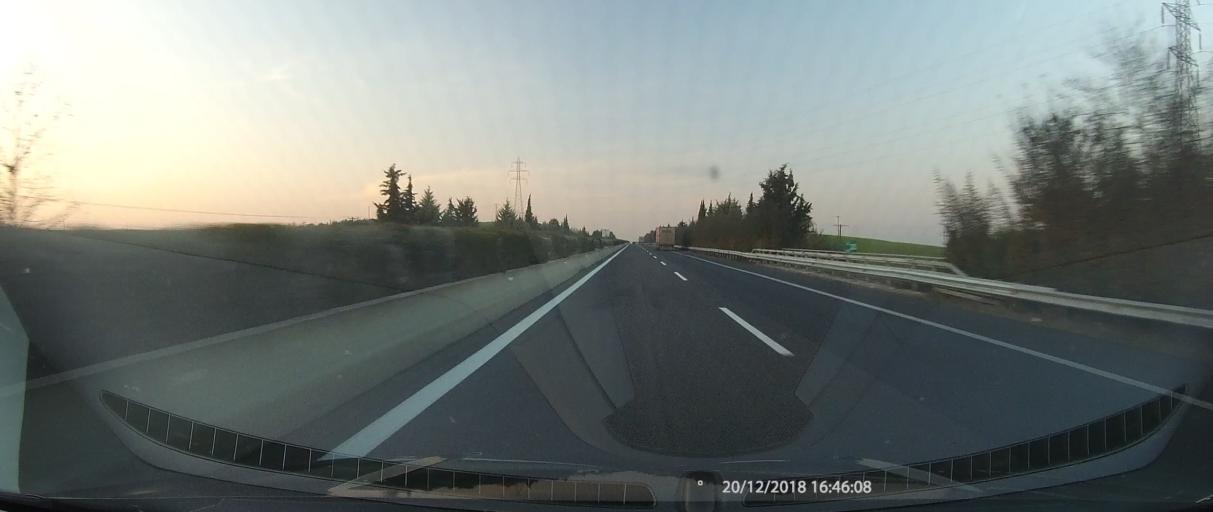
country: GR
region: Thessaly
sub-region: Nomos Magnisias
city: Stefanoviki
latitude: 39.4536
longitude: 22.6780
